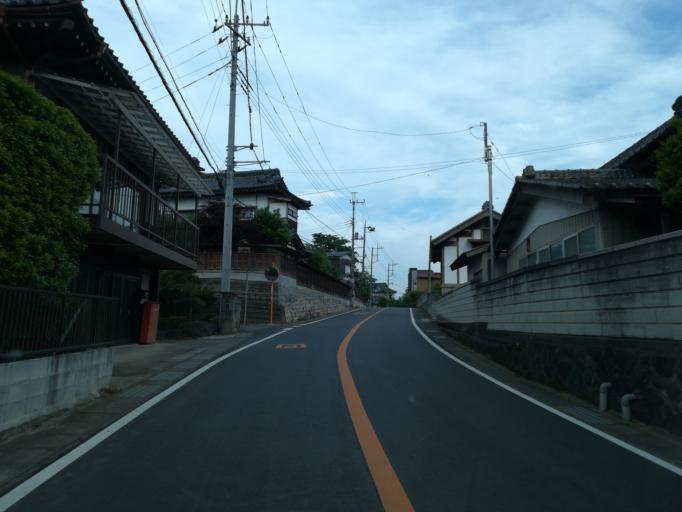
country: JP
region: Ibaraki
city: Tsukuba
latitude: 36.2242
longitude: 140.1539
